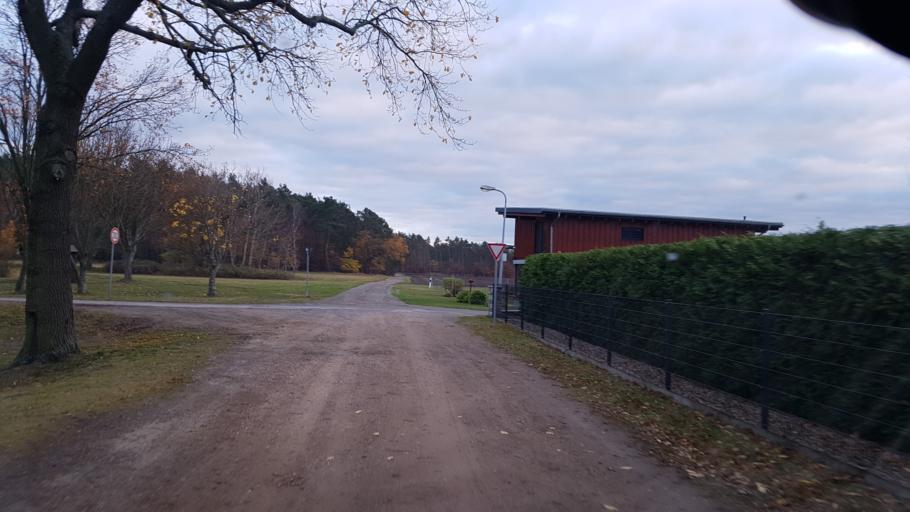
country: DE
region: Brandenburg
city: Kroppen
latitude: 51.4134
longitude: 13.7756
